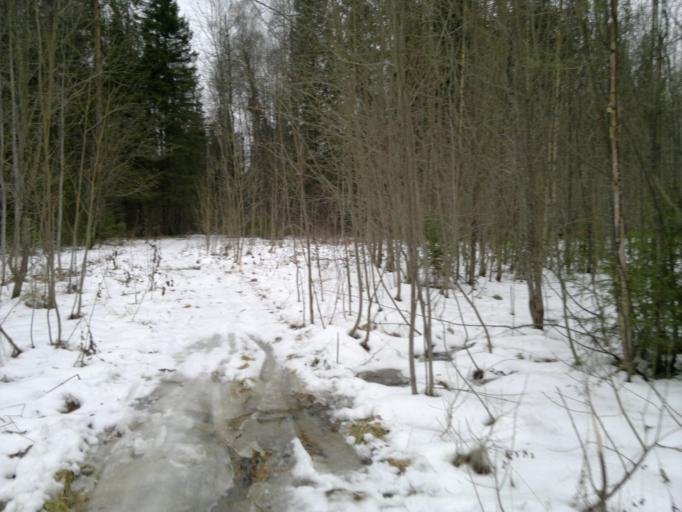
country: RU
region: Mariy-El
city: Yoshkar-Ola
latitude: 56.6054
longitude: 47.9620
